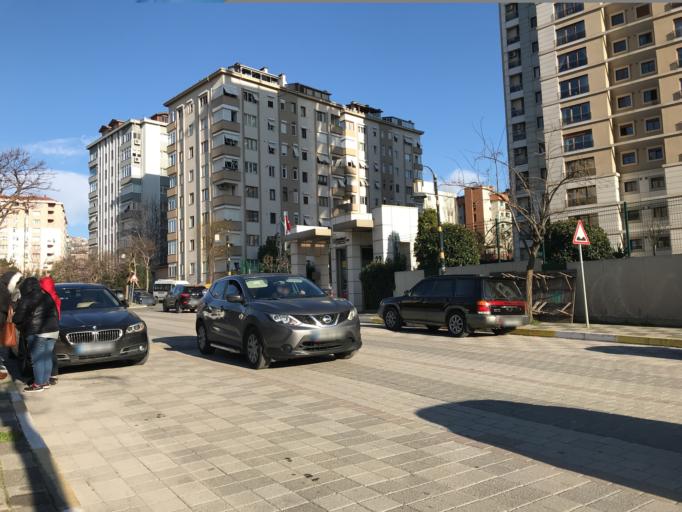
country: TR
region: Istanbul
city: Maltepe
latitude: 40.9321
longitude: 29.1324
